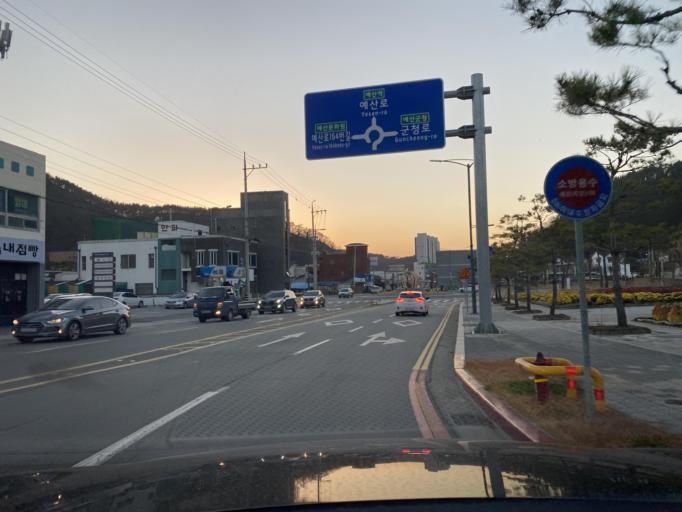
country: KR
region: Chungcheongnam-do
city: Yesan
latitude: 36.6786
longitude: 126.8444
